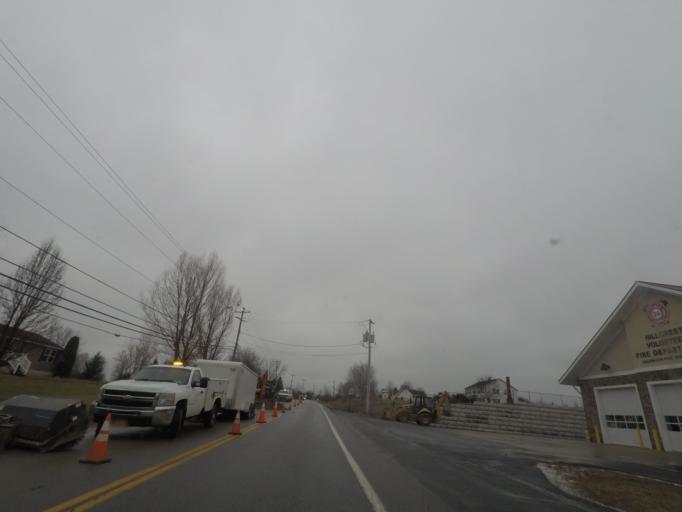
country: US
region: New York
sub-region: Saratoga County
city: Mechanicville
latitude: 42.8974
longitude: -73.7175
